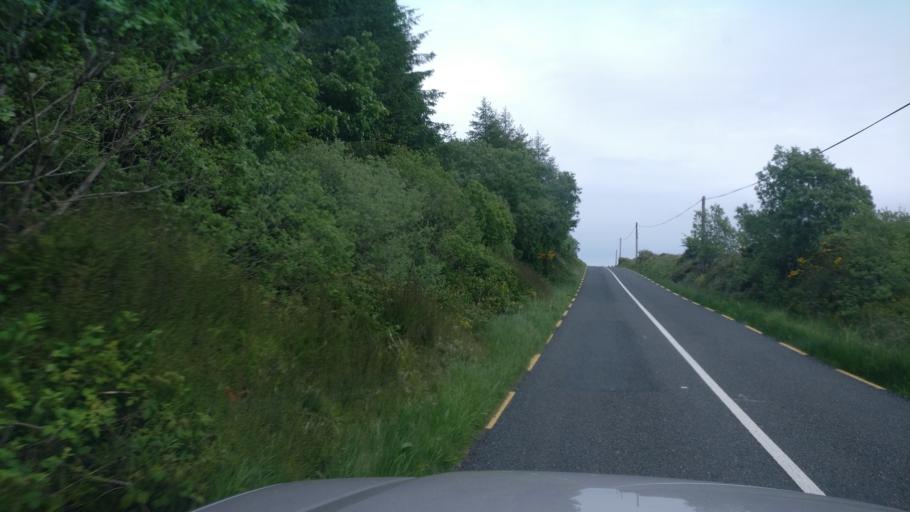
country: IE
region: Connaught
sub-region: County Galway
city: Gort
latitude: 53.0592
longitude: -8.6769
